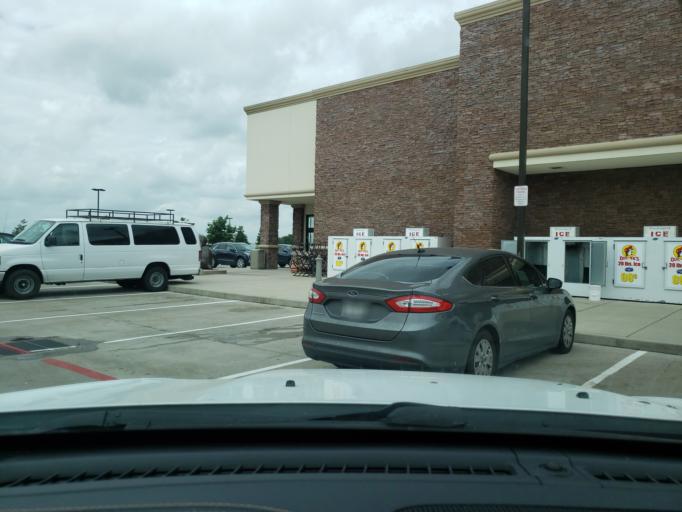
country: US
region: Texas
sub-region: Harris County
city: Katy
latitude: 29.7784
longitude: -95.8479
